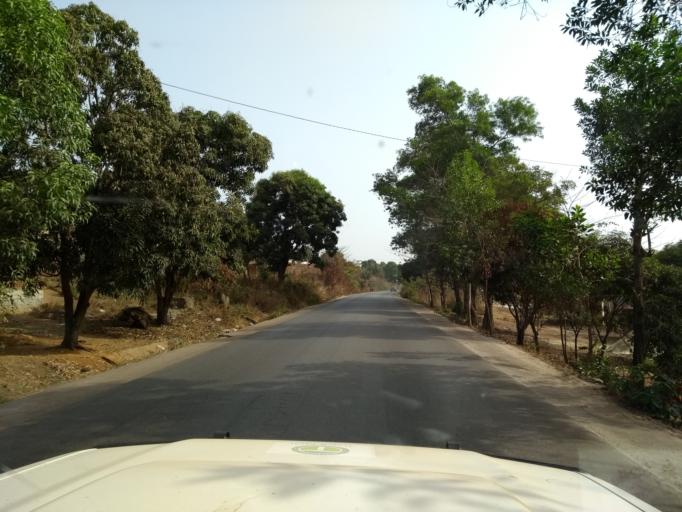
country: GN
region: Kindia
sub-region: Prefecture de Dubreka
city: Dubreka
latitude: 9.8442
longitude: -13.4871
